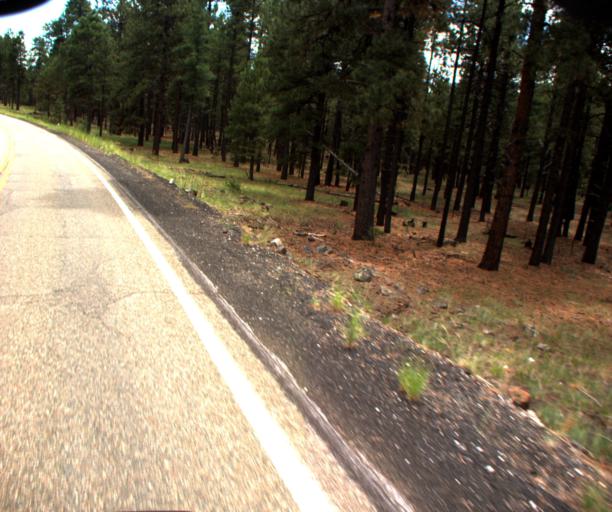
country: US
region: Arizona
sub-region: Coconino County
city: Flagstaff
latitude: 35.2967
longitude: -111.7657
